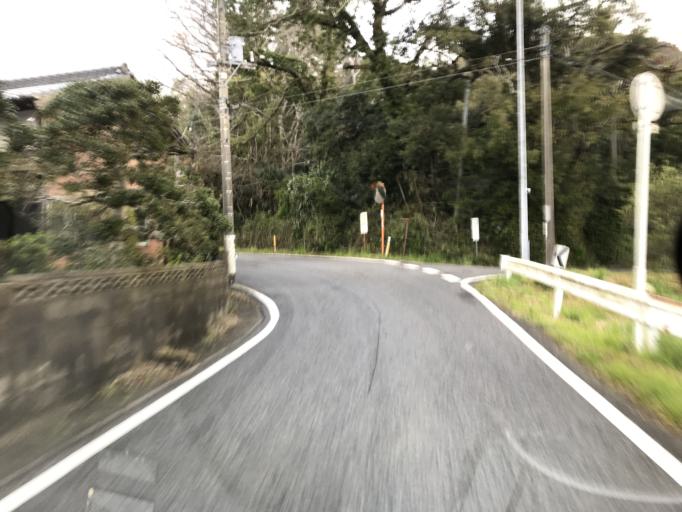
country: JP
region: Chiba
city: Yokaichiba
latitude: 35.7798
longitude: 140.5661
